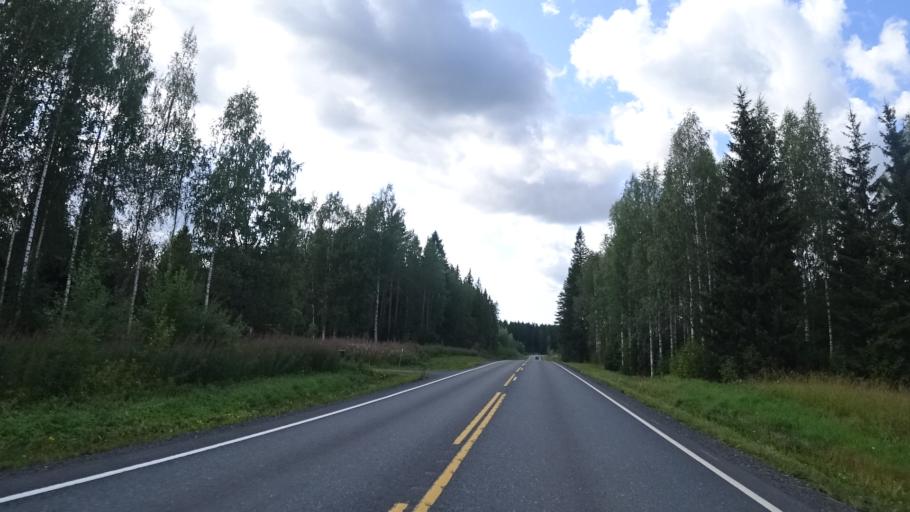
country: FI
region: North Karelia
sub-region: Keski-Karjala
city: Tohmajaervi
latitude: 62.1768
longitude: 30.5327
